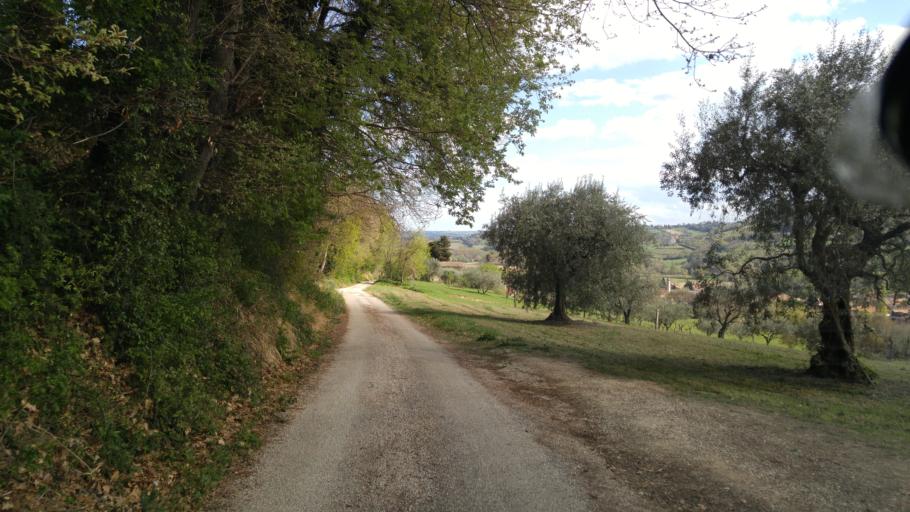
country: IT
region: The Marches
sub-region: Provincia di Pesaro e Urbino
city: Fenile
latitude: 43.8456
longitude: 12.9620
